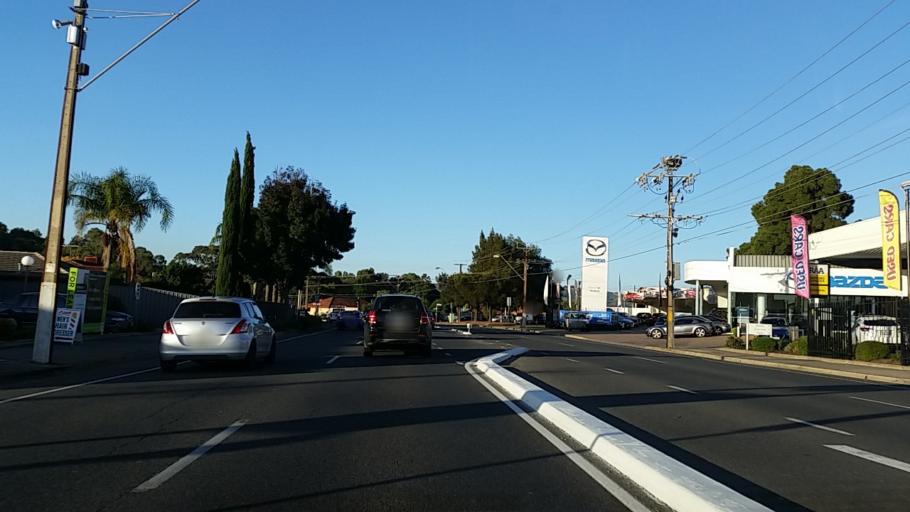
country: AU
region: South Australia
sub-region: Campbelltown
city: Paradise
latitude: -34.8700
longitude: 138.6746
